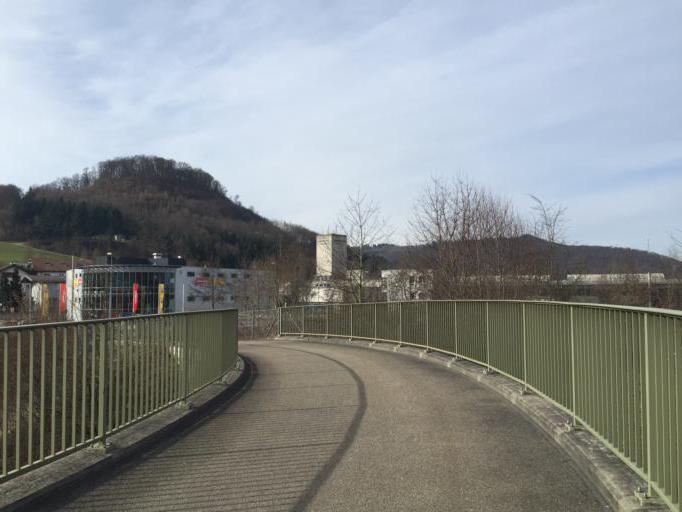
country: CH
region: Basel-Landschaft
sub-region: Bezirk Sissach
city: Sissach
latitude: 47.4625
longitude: 7.8254
